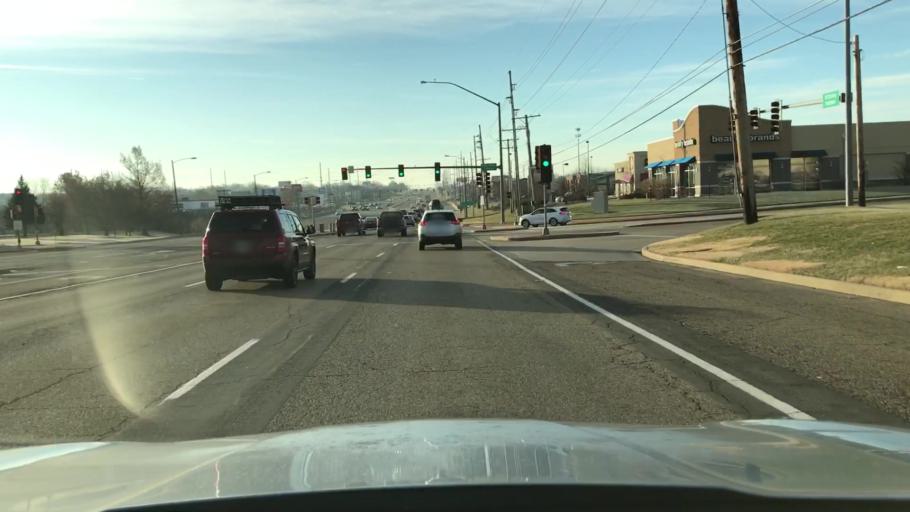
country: US
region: Illinois
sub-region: McLean County
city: Normal
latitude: 40.5069
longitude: -88.9534
